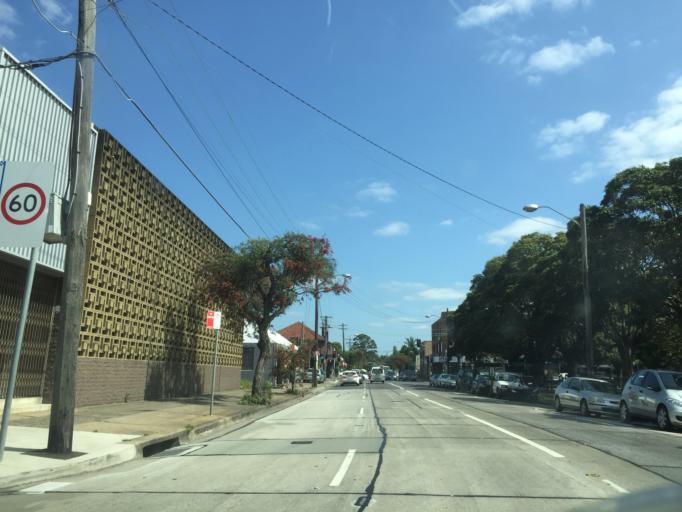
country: AU
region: New South Wales
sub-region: Marrickville
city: Marrickville
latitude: -33.9102
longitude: 151.1630
